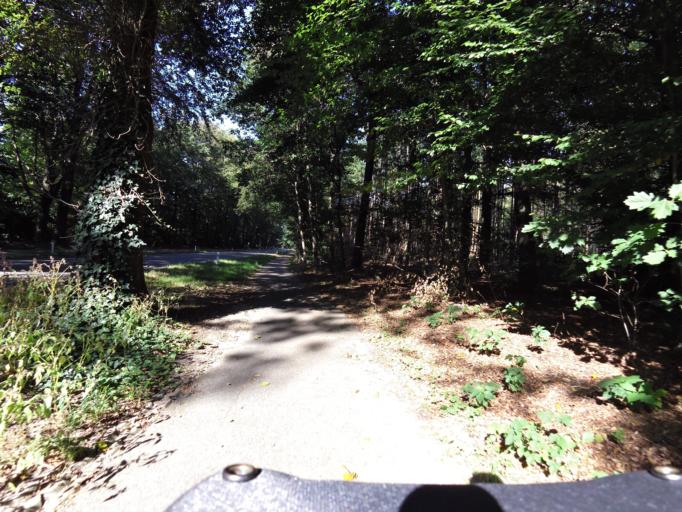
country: NL
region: Gelderland
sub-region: Gemeente Apeldoorn
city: Apeldoorn
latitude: 52.2167
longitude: 5.9199
